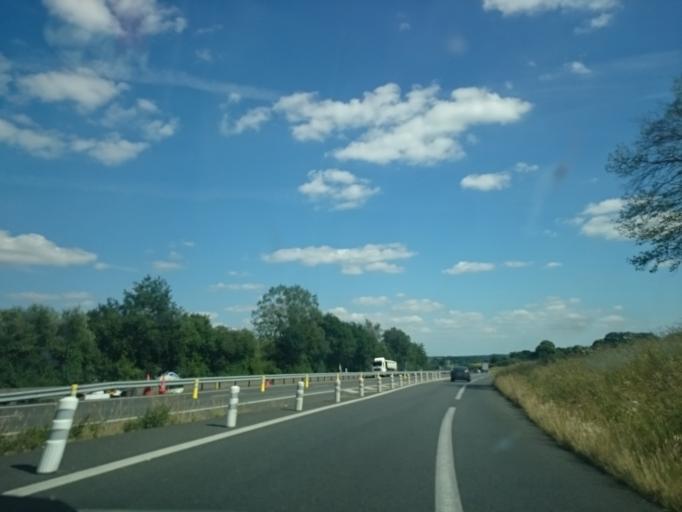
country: FR
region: Brittany
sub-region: Departement des Cotes-d'Armor
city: Loudeac
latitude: 48.1901
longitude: -2.7489
